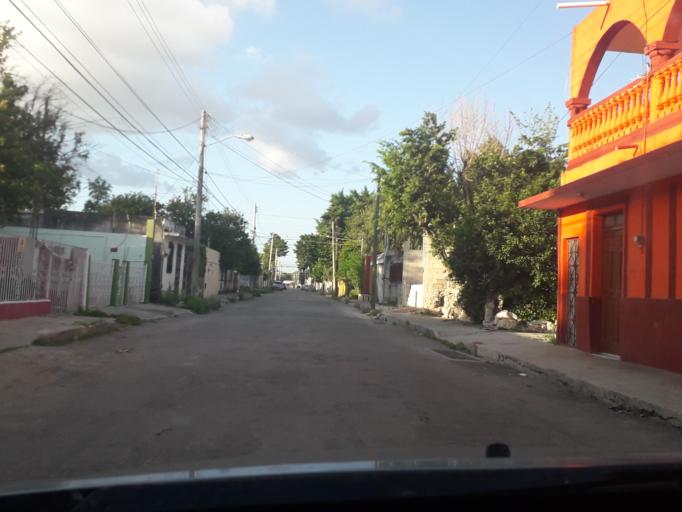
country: MX
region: Yucatan
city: Merida
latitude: 20.9673
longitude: -89.6458
